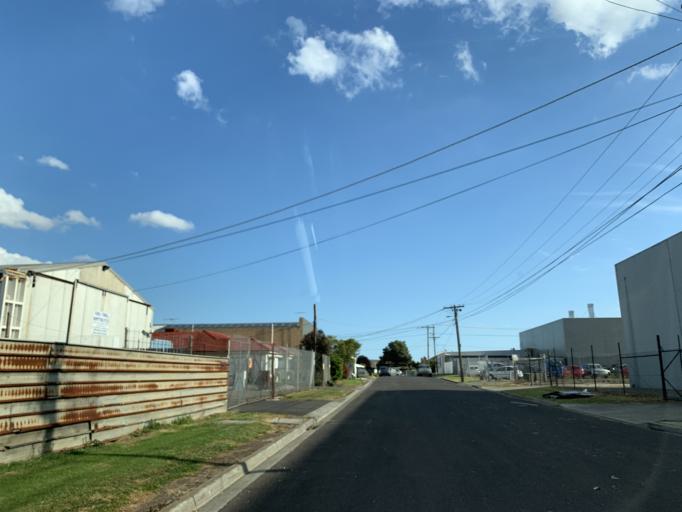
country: AU
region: Victoria
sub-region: Brimbank
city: Albion
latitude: -37.7645
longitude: 144.8437
